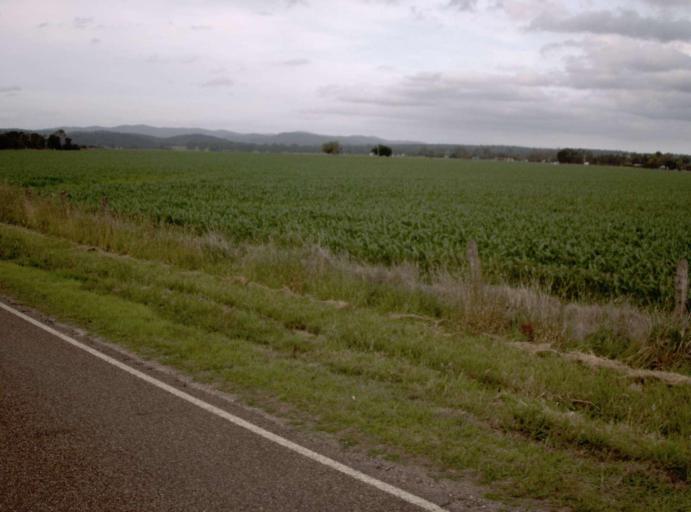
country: AU
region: Victoria
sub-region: Wellington
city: Sale
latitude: -37.8459
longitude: 147.0550
